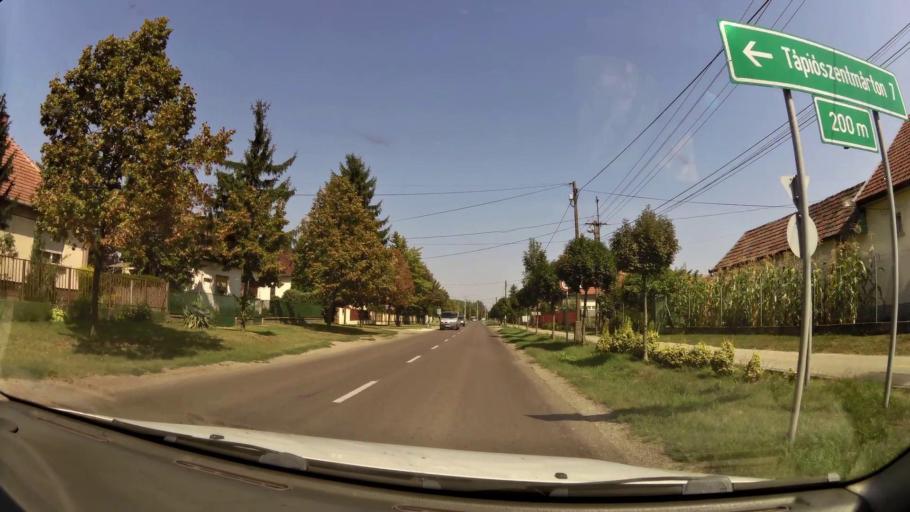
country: HU
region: Pest
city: Tapioszolos
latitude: 47.3089
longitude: 19.8722
